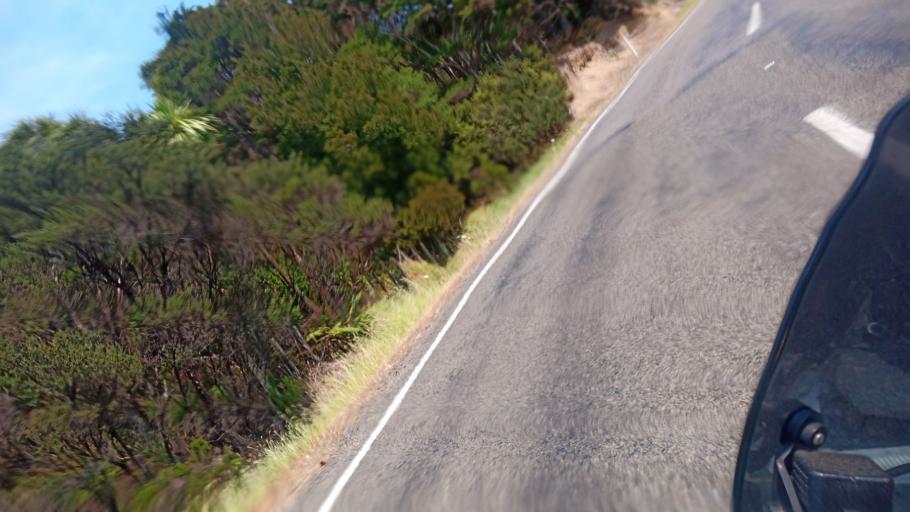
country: NZ
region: Bay of Plenty
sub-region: Opotiki District
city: Opotiki
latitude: -37.5940
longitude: 178.2228
